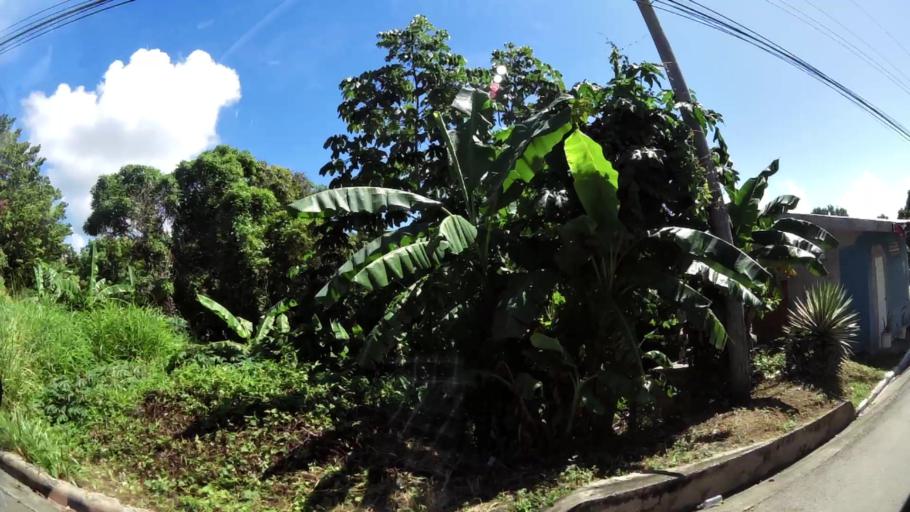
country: TT
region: Tobago
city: Scarborough
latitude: 11.1836
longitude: -60.7815
